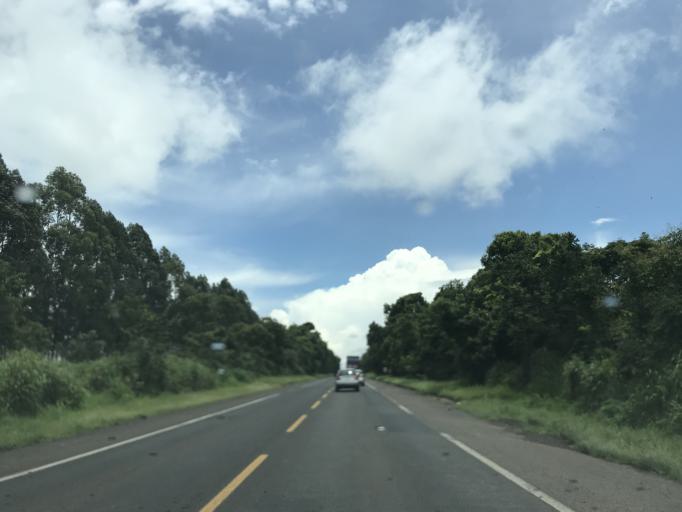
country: BR
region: Minas Gerais
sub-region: Frutal
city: Frutal
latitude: -19.6979
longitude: -48.9829
